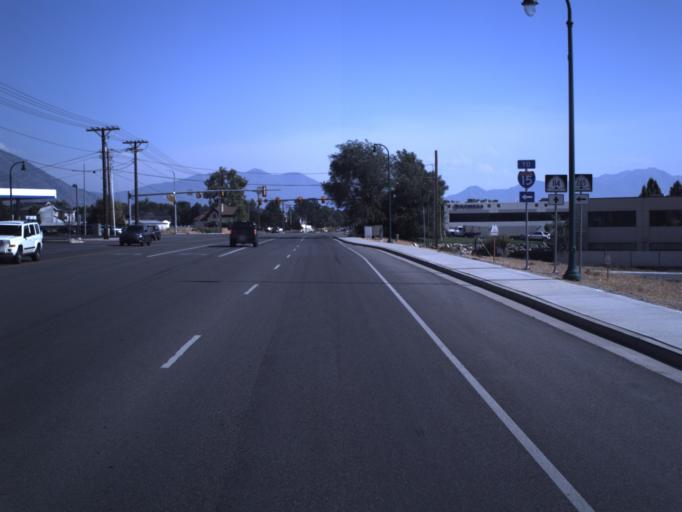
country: US
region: Utah
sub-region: Utah County
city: Orem
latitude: 40.2762
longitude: -111.7284
